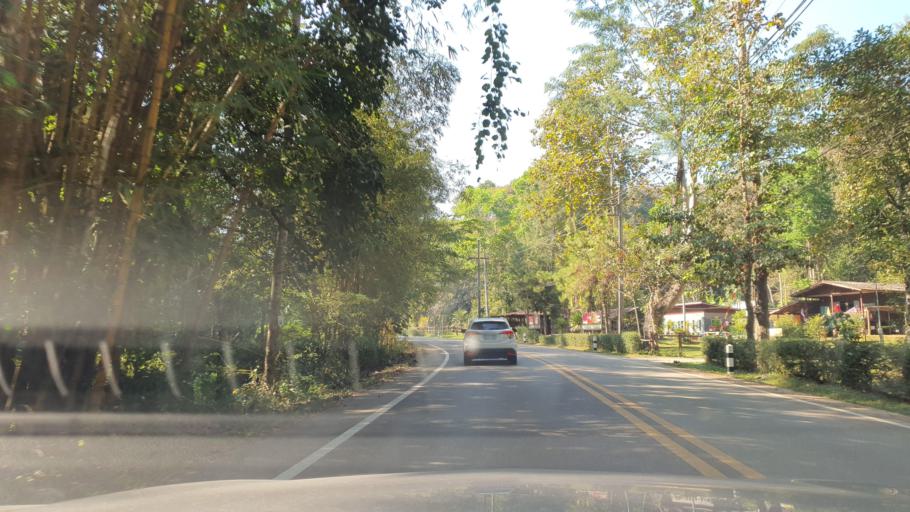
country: TH
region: Chiang Rai
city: Mae Lao
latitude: 19.8674
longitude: 99.6485
